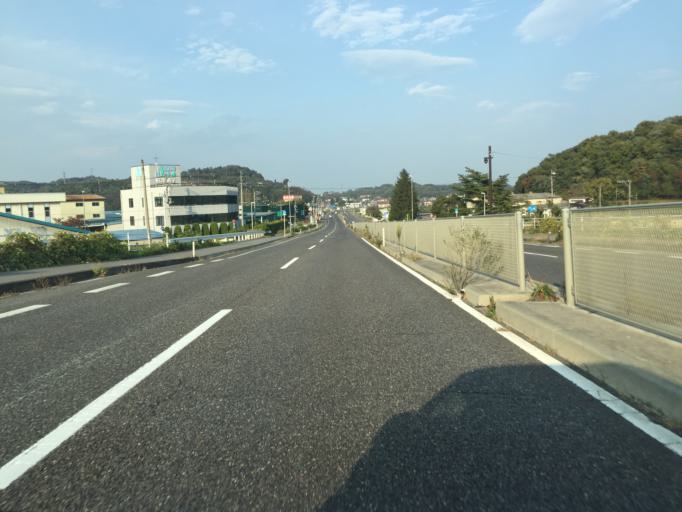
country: JP
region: Fukushima
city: Nihommatsu
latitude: 37.5570
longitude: 140.4046
